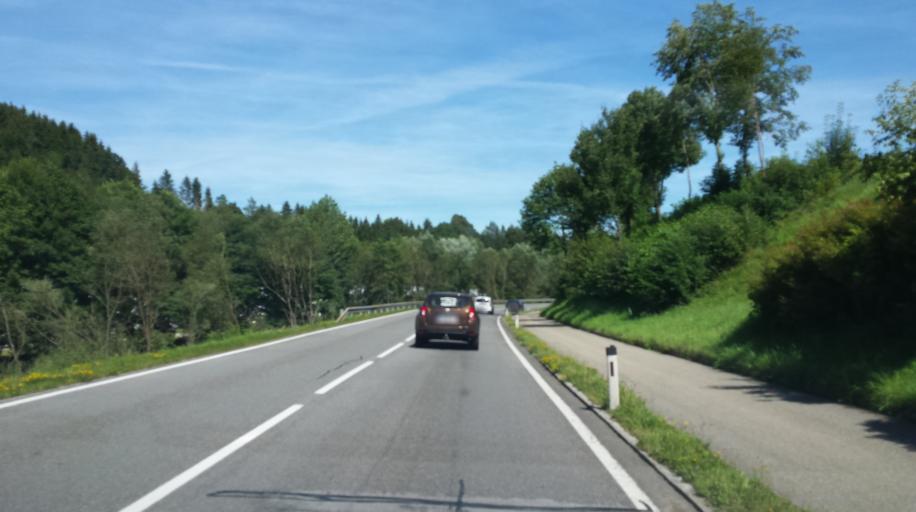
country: AT
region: Upper Austria
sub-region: Politischer Bezirk Vocklabruck
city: Frankenmarkt
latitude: 47.9888
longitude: 13.3947
